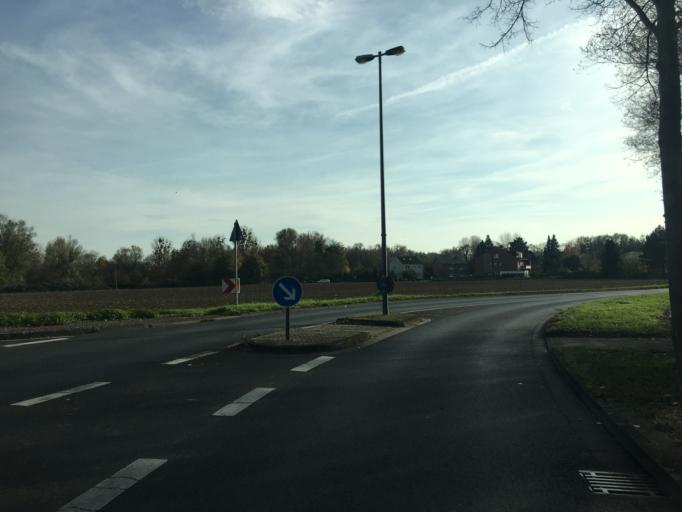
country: DE
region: North Rhine-Westphalia
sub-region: Regierungsbezirk Koln
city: Merheim
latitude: 50.9573
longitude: 7.0508
